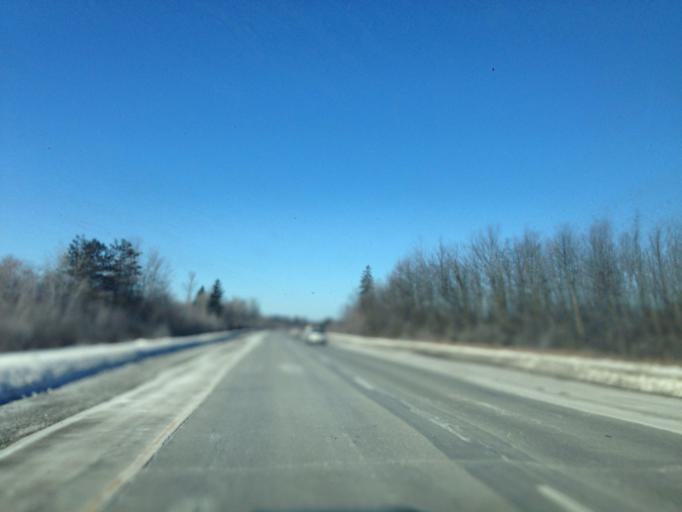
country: CA
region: Ontario
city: Ottawa
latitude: 45.3507
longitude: -75.4525
